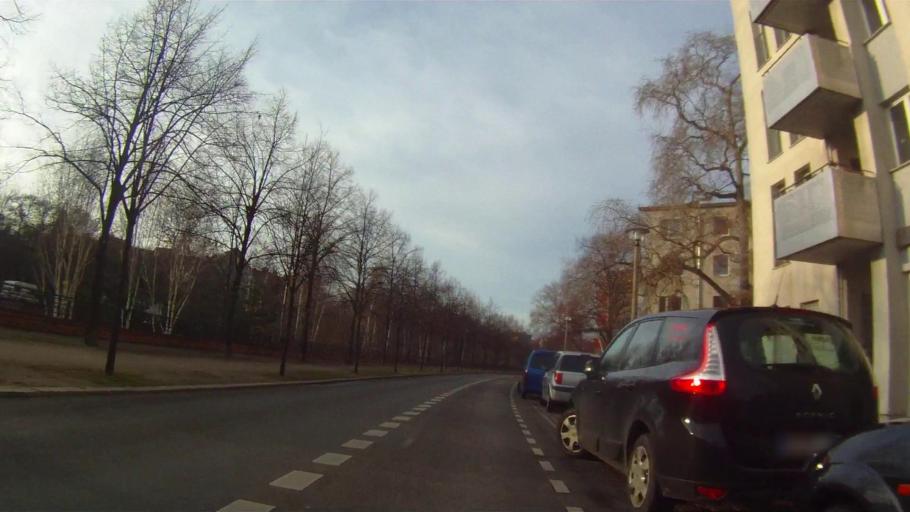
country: DE
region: Berlin
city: Berlin Treptow
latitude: 52.5060
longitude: 13.4259
